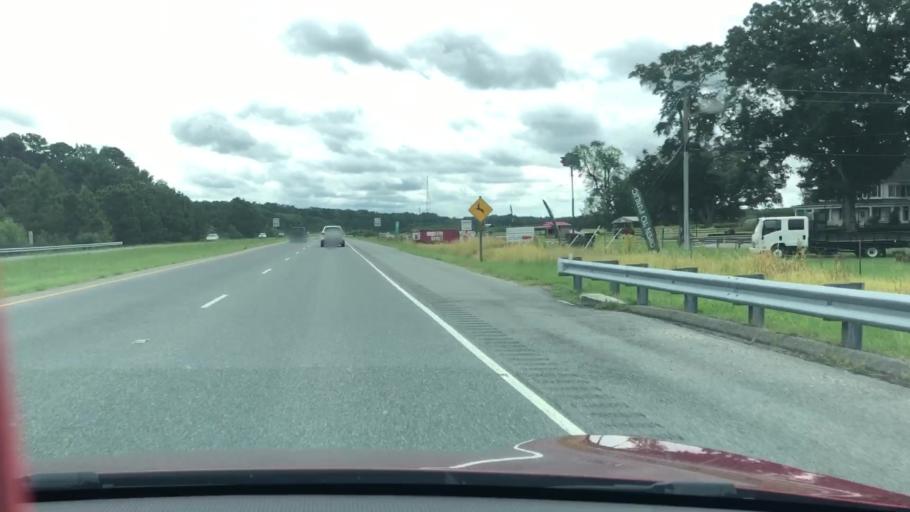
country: US
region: North Carolina
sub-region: Currituck County
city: Moyock
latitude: 36.6497
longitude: -76.2248
